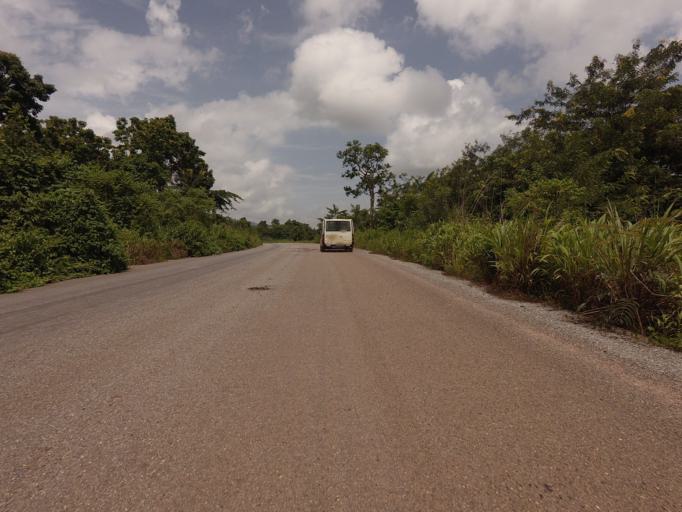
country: GH
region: Volta
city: Kpandu
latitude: 6.8044
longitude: 0.3733
